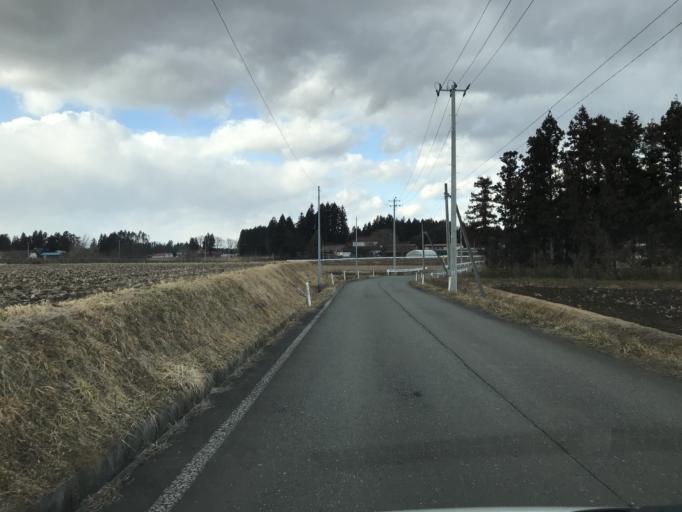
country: JP
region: Iwate
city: Mizusawa
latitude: 39.0801
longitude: 141.1114
